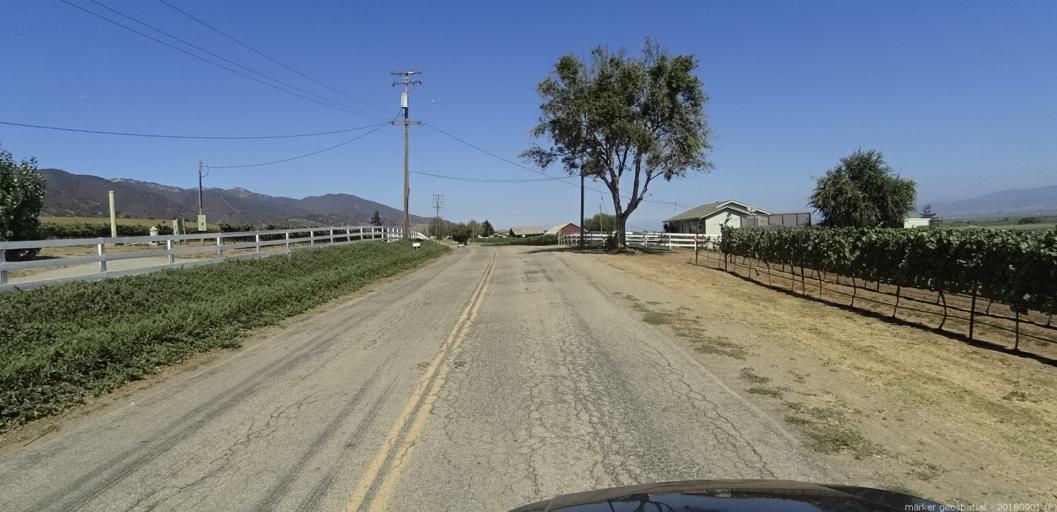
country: US
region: California
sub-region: Monterey County
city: Gonzales
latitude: 36.5032
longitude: -121.5063
